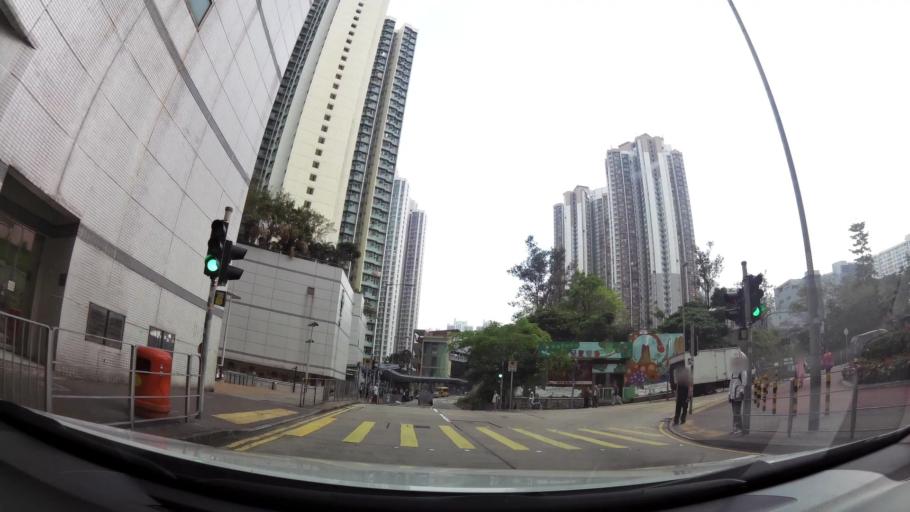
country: HK
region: Kowloon City
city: Kowloon
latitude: 22.3083
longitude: 114.2356
